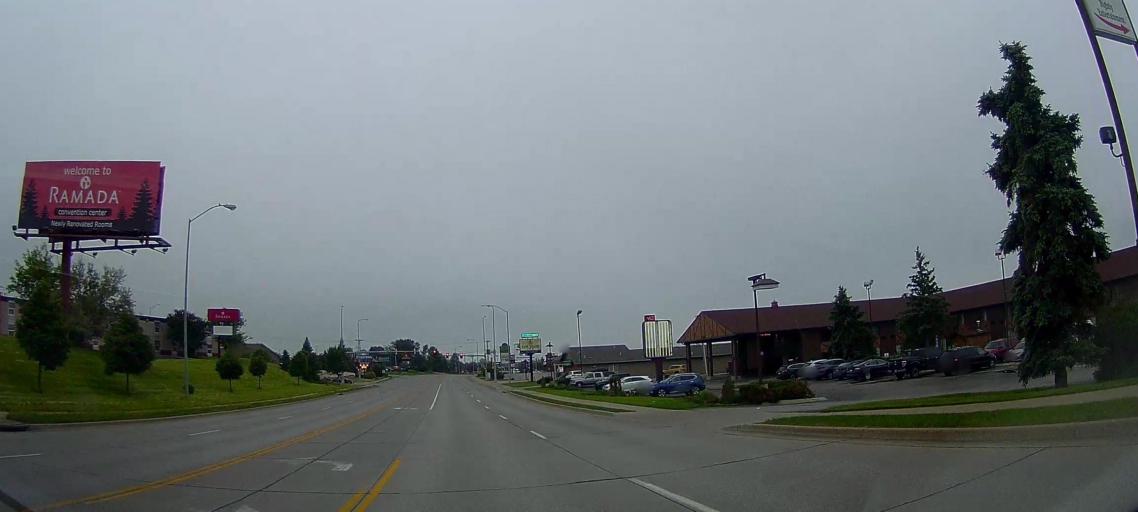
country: US
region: South Dakota
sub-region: Pennington County
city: Rapid City
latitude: 44.1017
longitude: -103.2034
